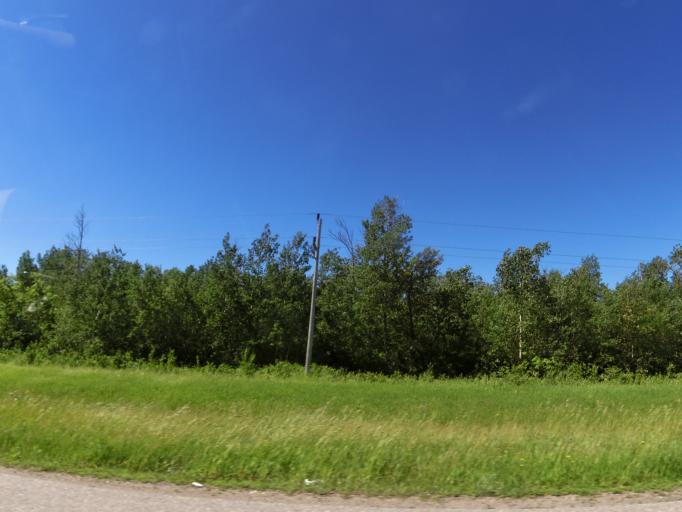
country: US
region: Minnesota
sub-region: Red Lake County
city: Red Lake Falls
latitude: 47.7214
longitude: -96.1856
